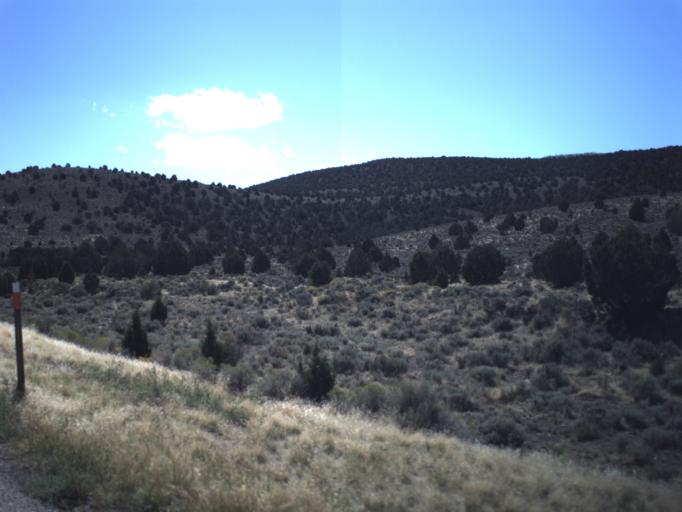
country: US
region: Utah
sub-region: Beaver County
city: Milford
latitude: 38.1278
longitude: -112.9575
